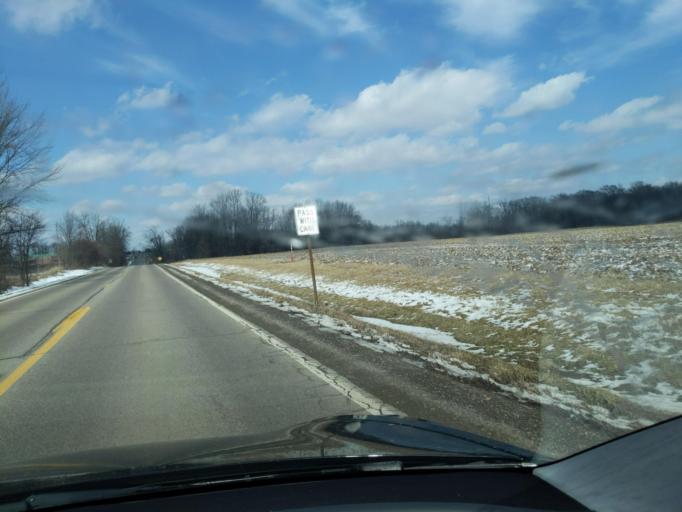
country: US
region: Michigan
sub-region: Livingston County
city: Fowlerville
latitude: 42.6391
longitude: -84.0722
